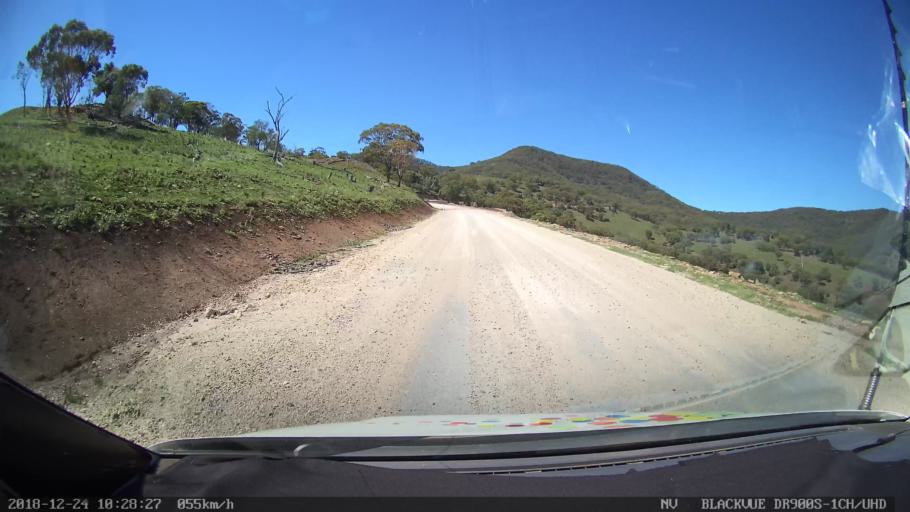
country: AU
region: New South Wales
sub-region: Liverpool Plains
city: Quirindi
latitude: -31.8262
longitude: 150.5311
